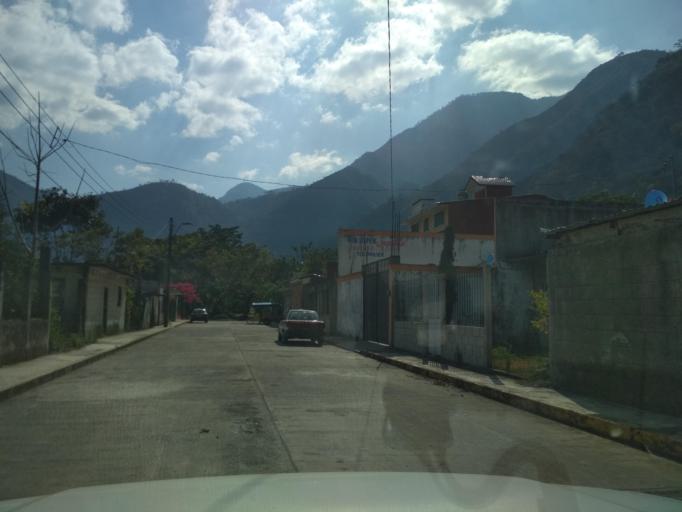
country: MX
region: Veracruz
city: Jalapilla
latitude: 18.8090
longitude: -97.0984
